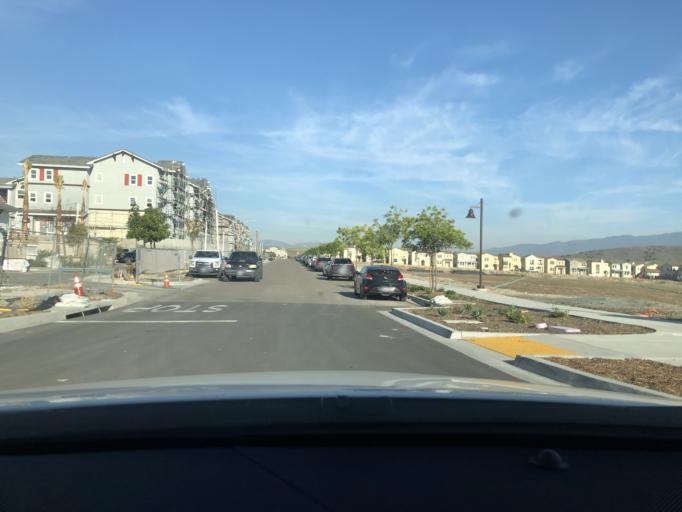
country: US
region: California
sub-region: San Diego County
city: Bonita
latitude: 32.5992
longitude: -116.9996
